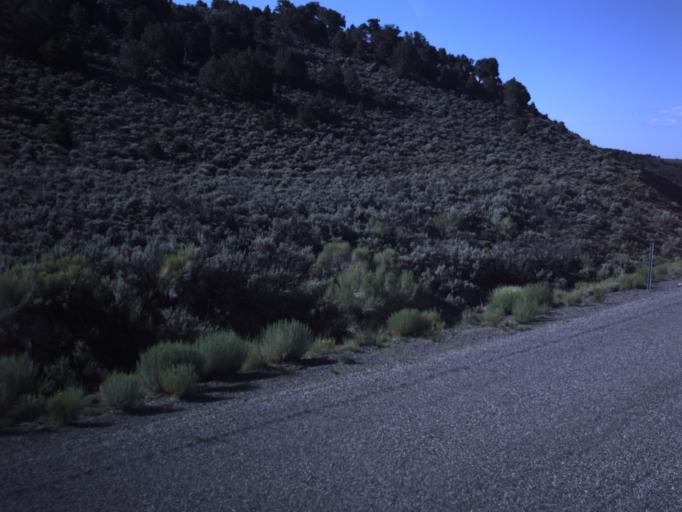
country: US
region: Utah
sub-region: Wayne County
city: Loa
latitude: 38.4825
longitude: -111.5508
